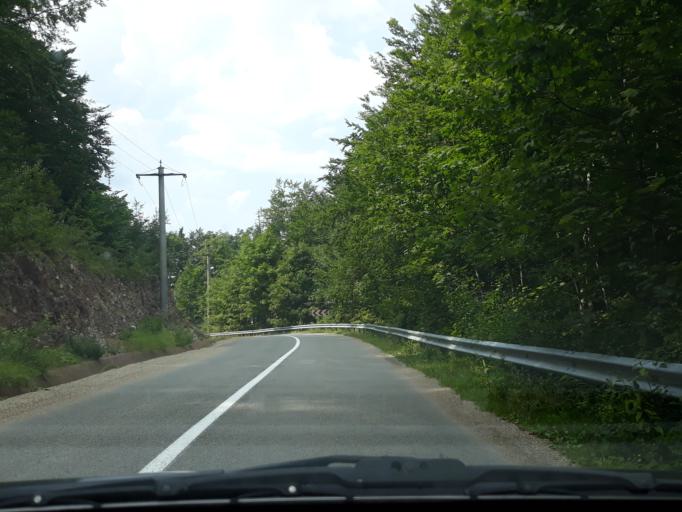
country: RO
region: Bihor
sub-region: Comuna Pietroasa
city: Pietroasa
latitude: 46.5932
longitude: 22.6801
